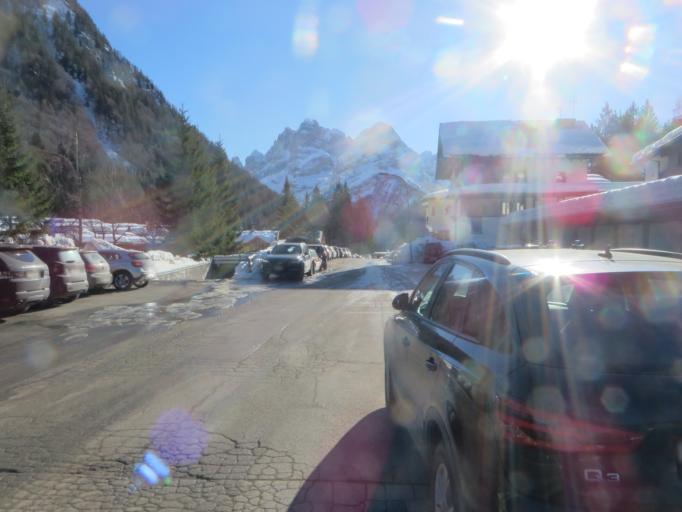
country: IT
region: Trentino-Alto Adige
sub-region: Provincia di Trento
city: Carisolo
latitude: 46.2180
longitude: 10.8238
